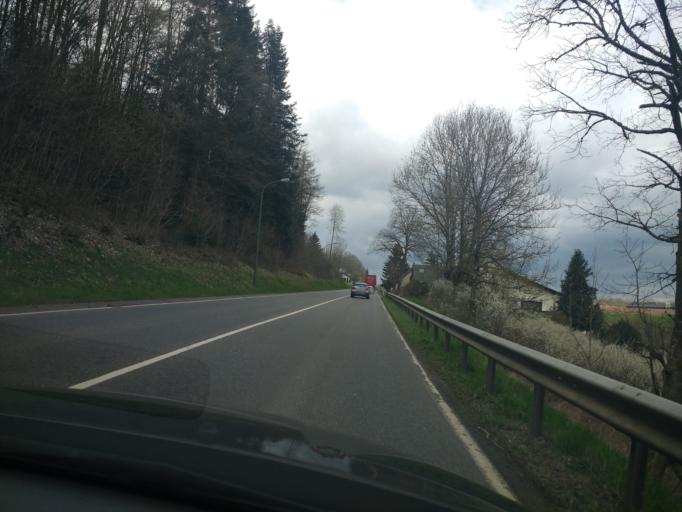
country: DE
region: Rheinland-Pfalz
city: Junkerath
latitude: 50.3482
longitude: 6.5660
